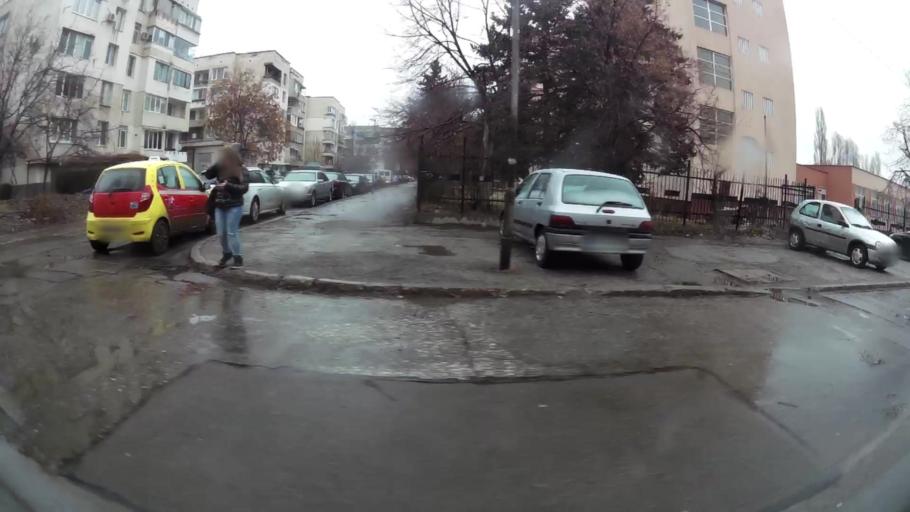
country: BG
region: Sofia-Capital
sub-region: Stolichna Obshtina
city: Sofia
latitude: 42.6689
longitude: 23.3873
